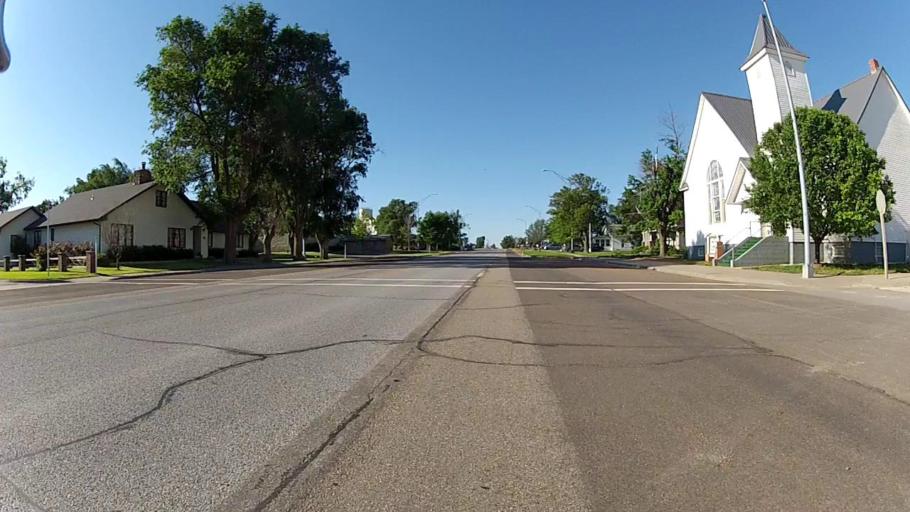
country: US
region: Kansas
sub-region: Ford County
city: Dodge City
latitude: 37.6376
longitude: -99.7539
